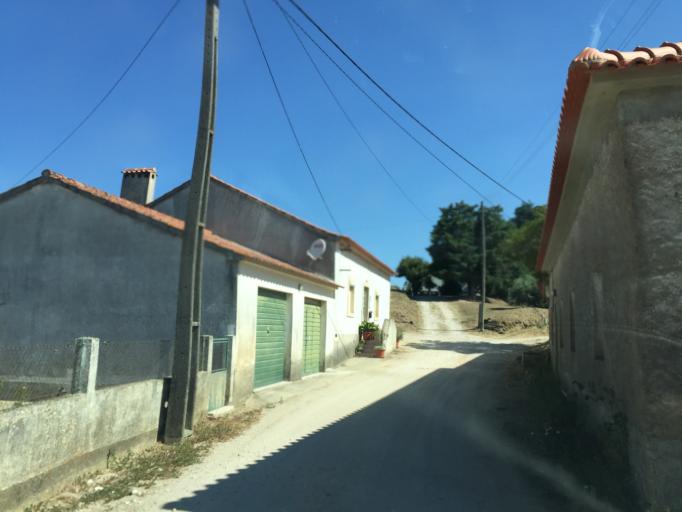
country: PT
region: Santarem
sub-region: Tomar
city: Tomar
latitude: 39.6052
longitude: -8.3489
